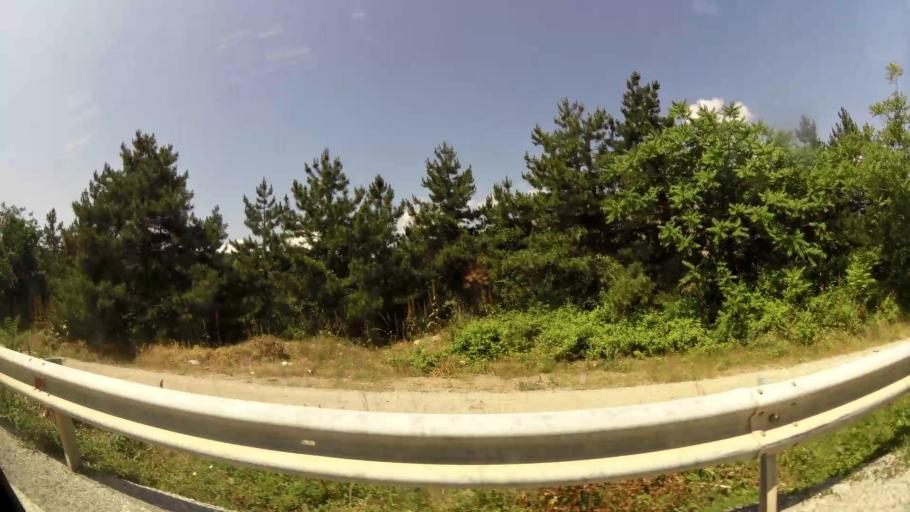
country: GR
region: West Macedonia
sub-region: Nomos Kozanis
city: Kozani
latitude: 40.3134
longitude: 21.7836
